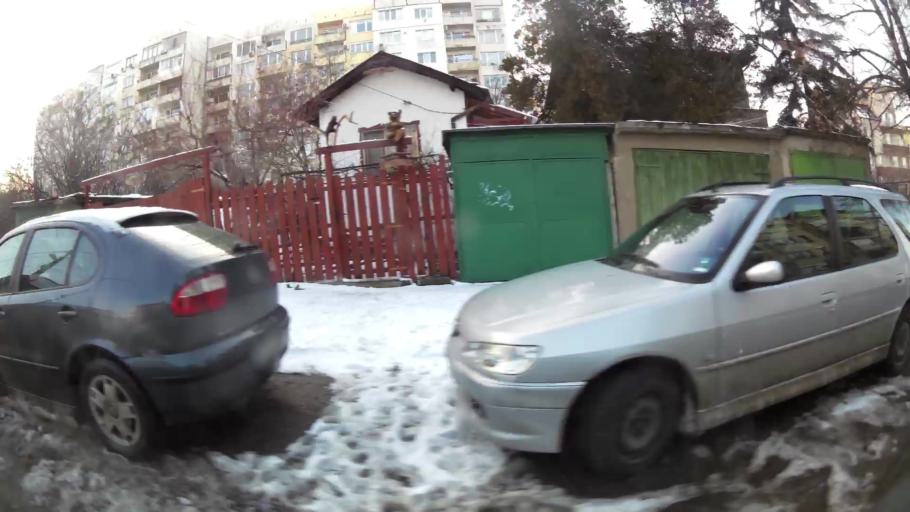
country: BG
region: Sofia-Capital
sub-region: Stolichna Obshtina
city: Sofia
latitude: 42.6936
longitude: 23.3636
